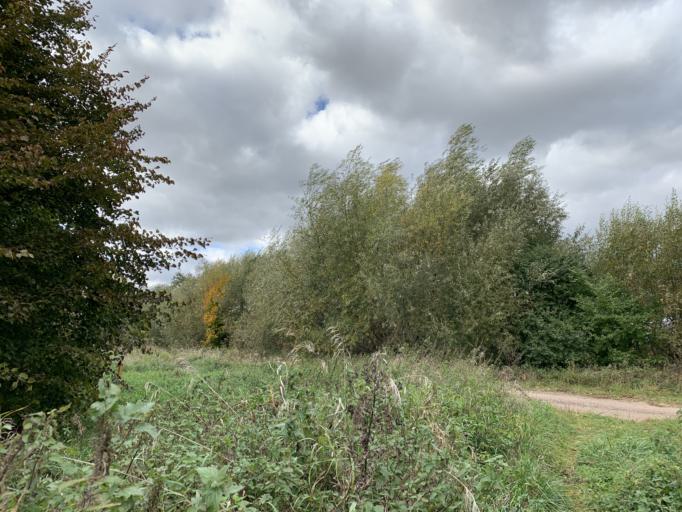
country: BY
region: Minsk
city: Nyasvizh
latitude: 53.2350
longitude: 26.7091
